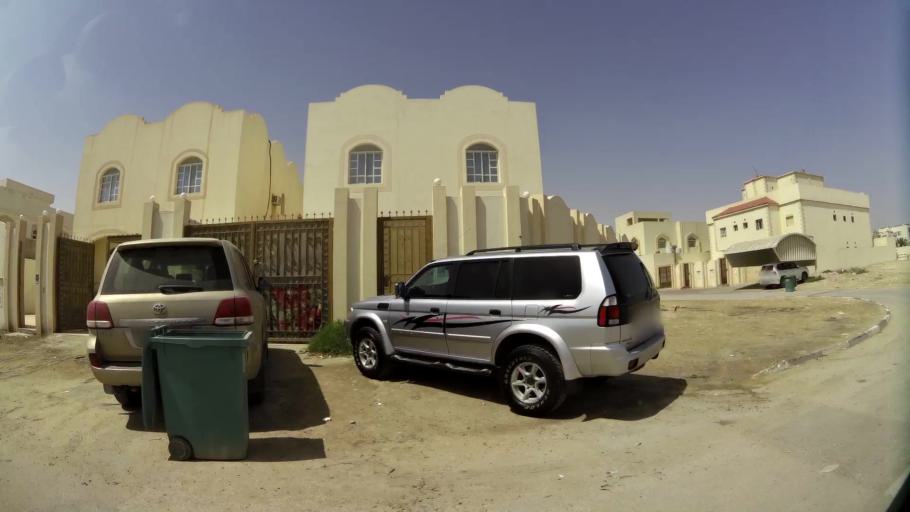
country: QA
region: Baladiyat Umm Salal
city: Umm Salal Muhammad
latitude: 25.3747
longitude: 51.4236
